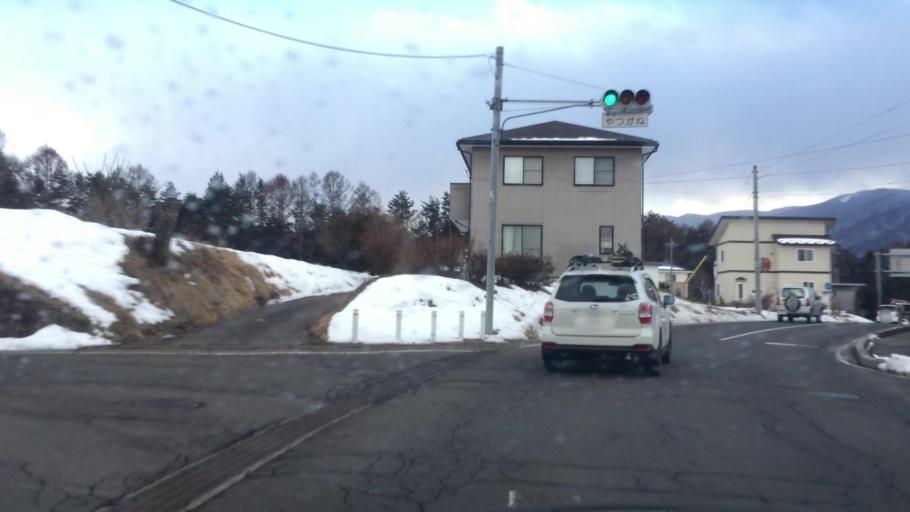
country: JP
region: Nagano
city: Chino
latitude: 35.9564
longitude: 138.2153
